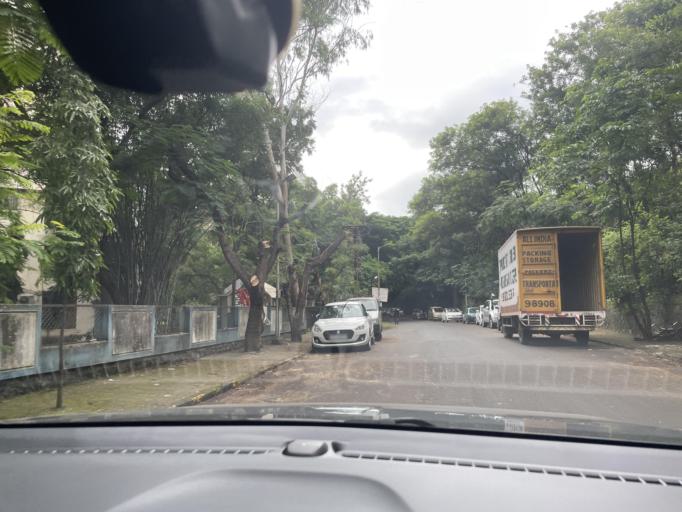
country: IN
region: Maharashtra
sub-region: Pune Division
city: Shivaji Nagar
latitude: 18.5315
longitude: 73.8144
